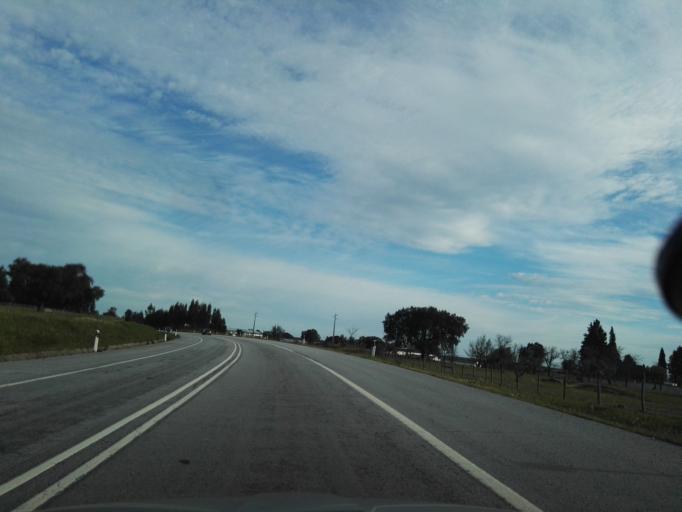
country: PT
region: Portalegre
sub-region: Nisa
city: Nisa
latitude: 39.4207
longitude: -7.7070
